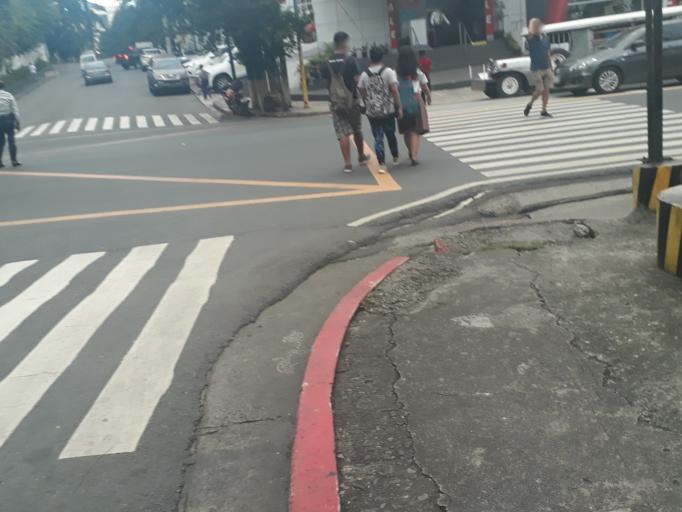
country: PH
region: Metro Manila
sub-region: Mandaluyong
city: Mandaluyong City
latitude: 14.5898
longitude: 121.0399
